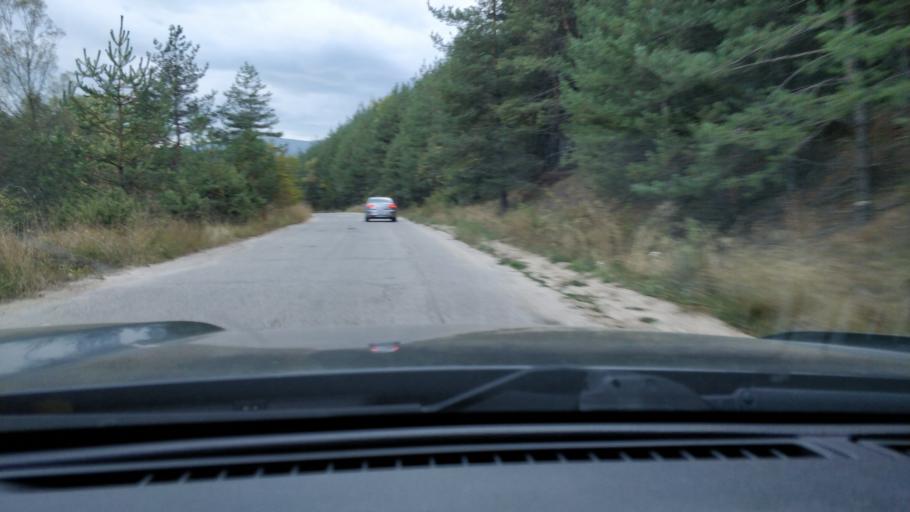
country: BG
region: Sofiya
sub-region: Obshtina Samokov
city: Samokov
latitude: 42.4820
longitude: 23.3921
